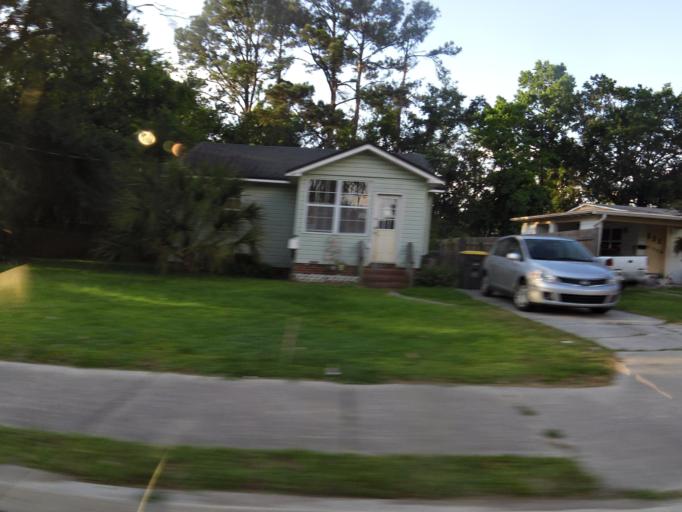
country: US
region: Florida
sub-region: Duval County
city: Jacksonville
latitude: 30.2920
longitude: -81.7328
